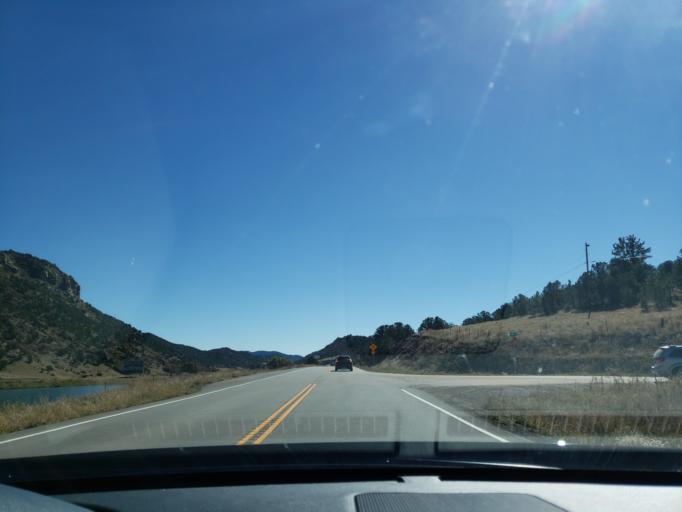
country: US
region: Colorado
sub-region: Fremont County
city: Canon City
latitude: 38.6119
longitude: -105.4417
